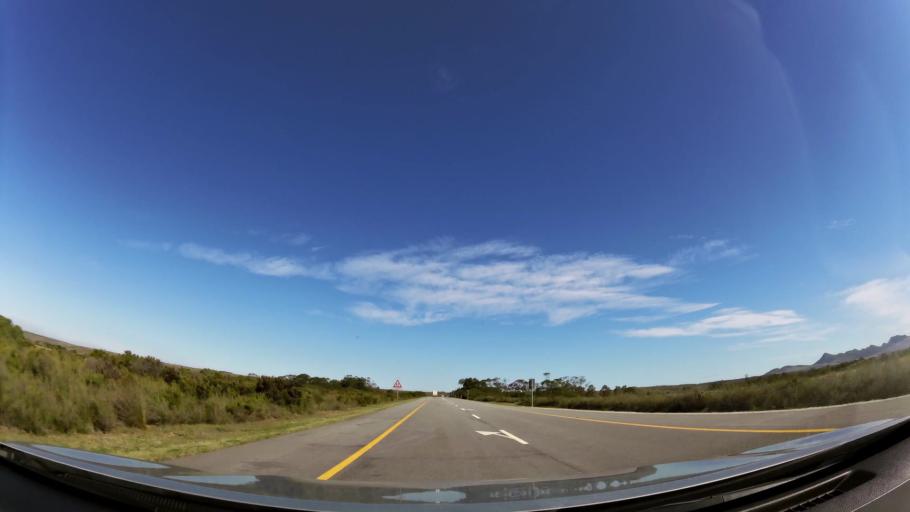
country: ZA
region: Eastern Cape
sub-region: Cacadu District Municipality
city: Kruisfontein
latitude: -34.0335
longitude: 24.5941
